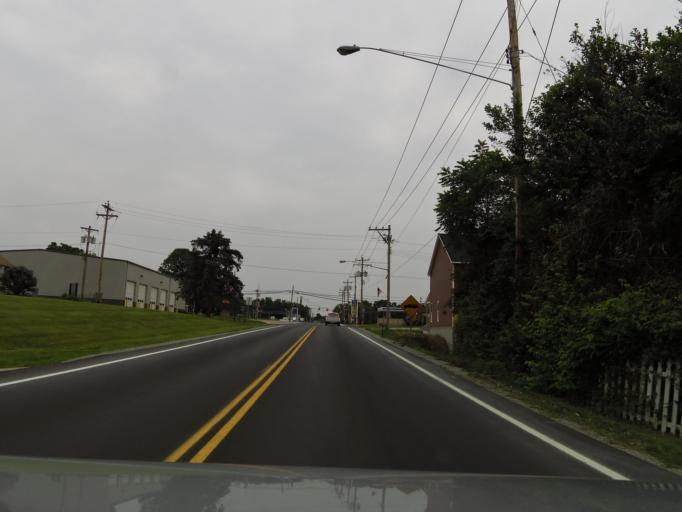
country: US
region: Ohio
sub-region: Clinton County
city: Blanchester
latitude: 39.1882
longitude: -83.9329
